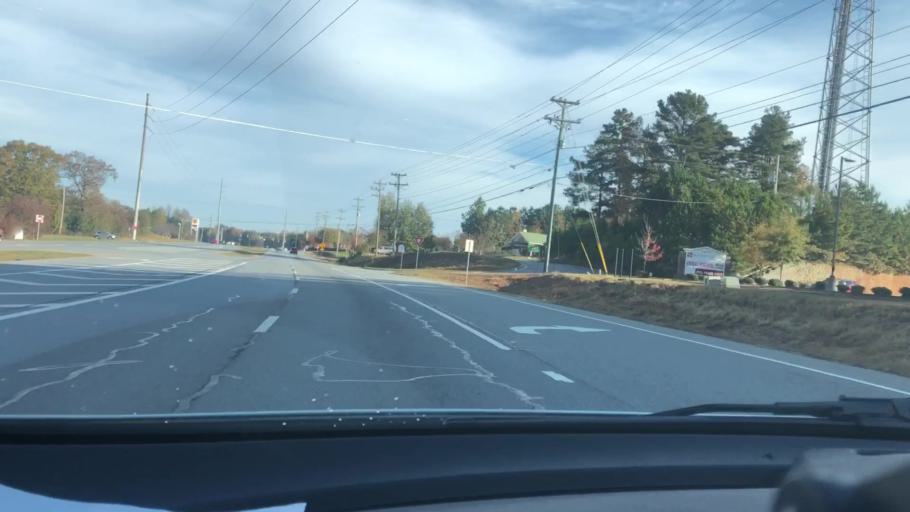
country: US
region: Georgia
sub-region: Forsyth County
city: Cumming
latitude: 34.1206
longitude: -84.1722
